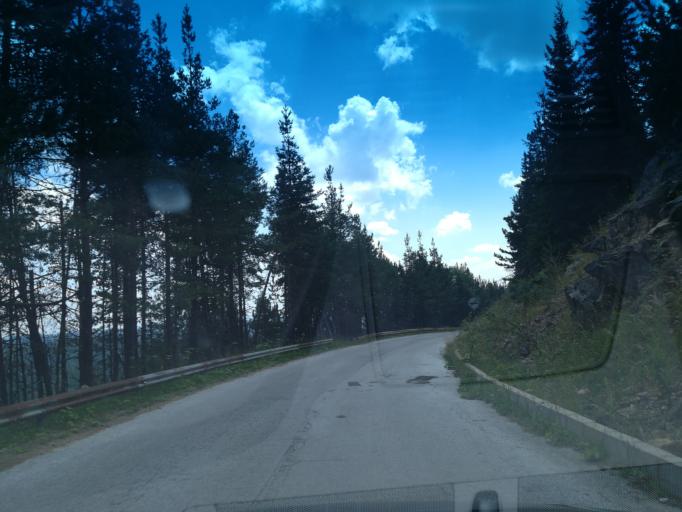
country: BG
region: Smolyan
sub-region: Obshtina Chepelare
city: Chepelare
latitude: 41.6859
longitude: 24.7528
